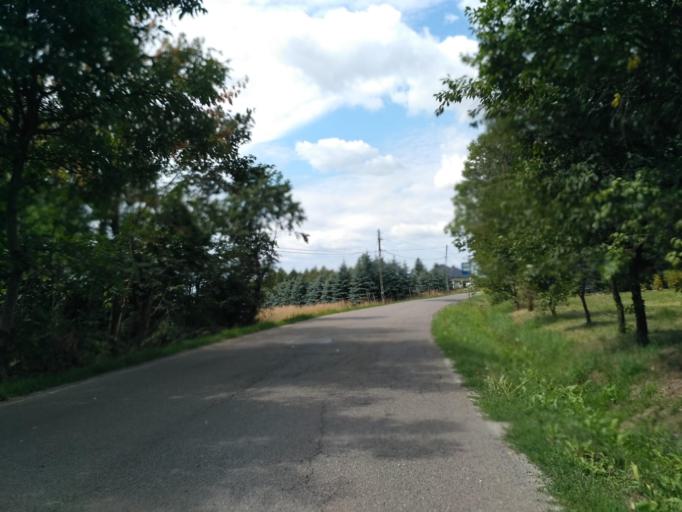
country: PL
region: Subcarpathian Voivodeship
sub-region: Powiat rzeszowski
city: Hyzne
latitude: 49.9396
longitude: 22.1710
